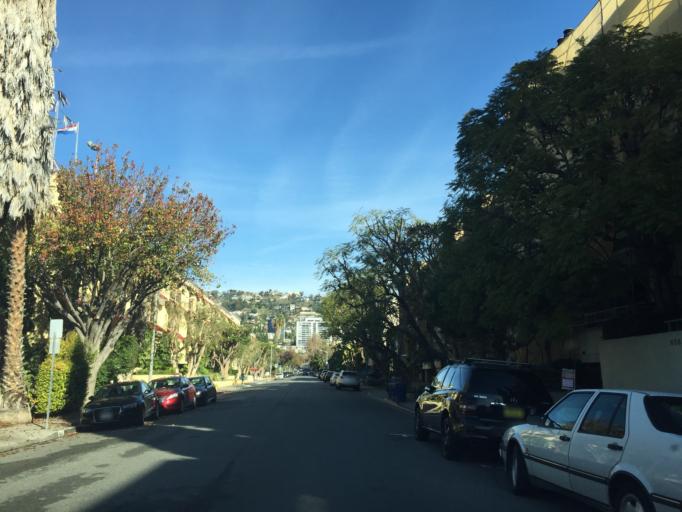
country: US
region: California
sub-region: Los Angeles County
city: West Hollywood
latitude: 34.0834
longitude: -118.3776
